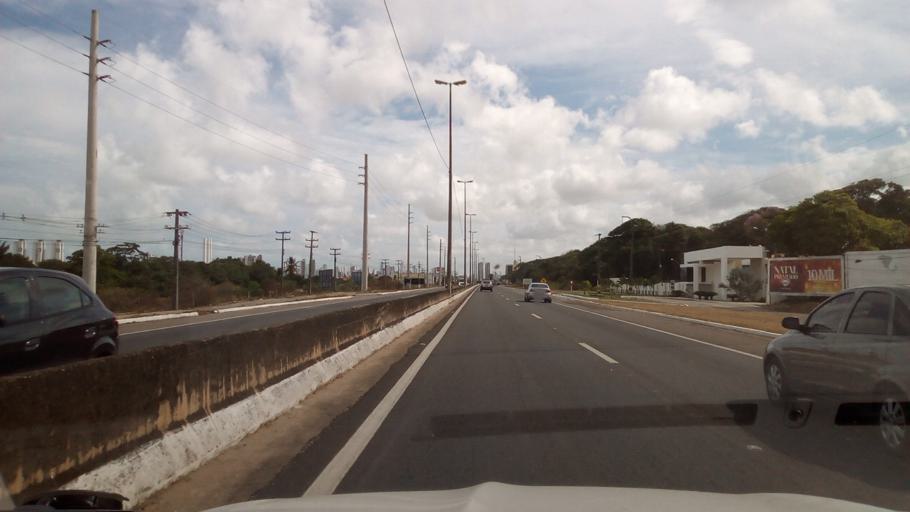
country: BR
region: Paraiba
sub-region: Joao Pessoa
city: Joao Pessoa
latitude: -7.0588
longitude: -34.8507
